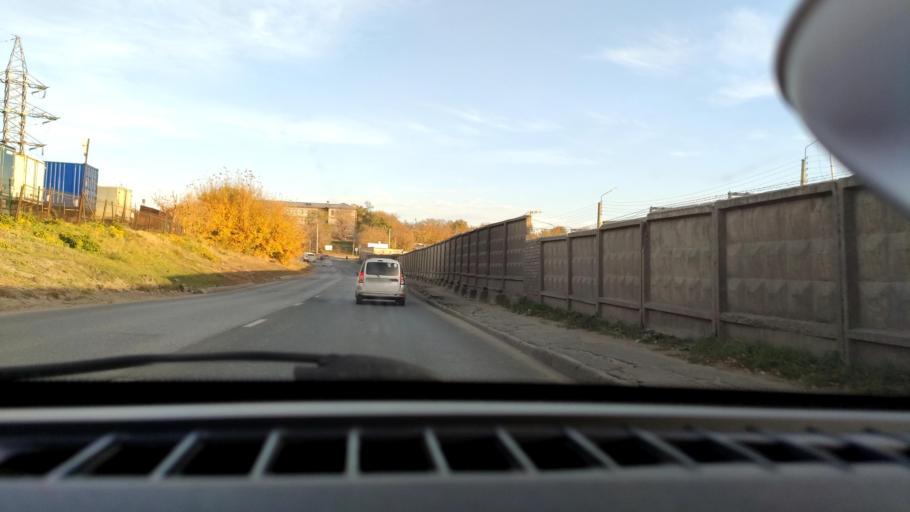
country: RU
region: Samara
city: Samara
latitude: 53.1860
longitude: 50.1408
